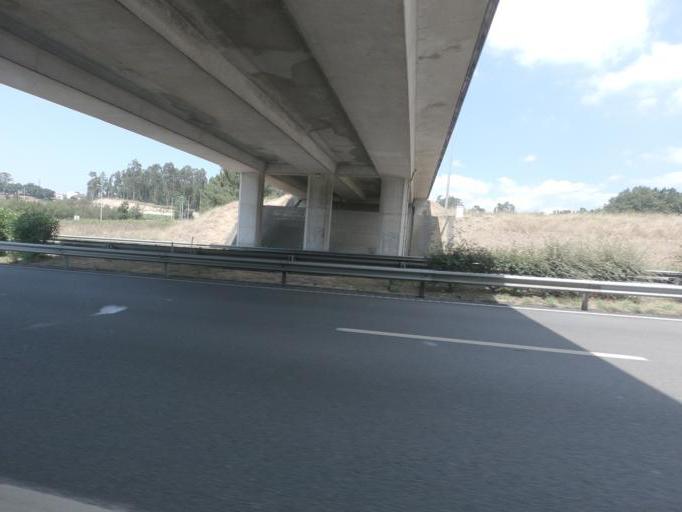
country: PT
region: Porto
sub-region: Paredes
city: Paredes
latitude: 41.2016
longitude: -8.3087
